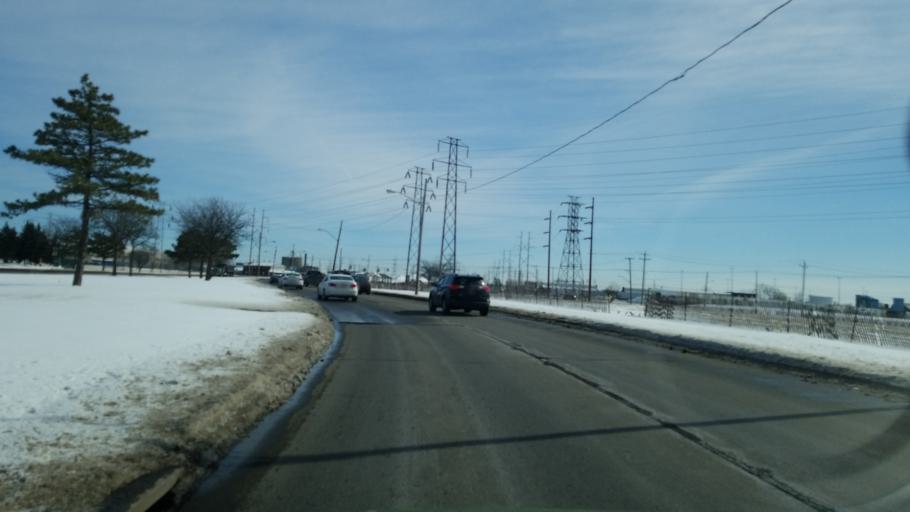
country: US
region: New York
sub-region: Niagara County
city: Niagara Falls
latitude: 43.0937
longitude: -79.0141
